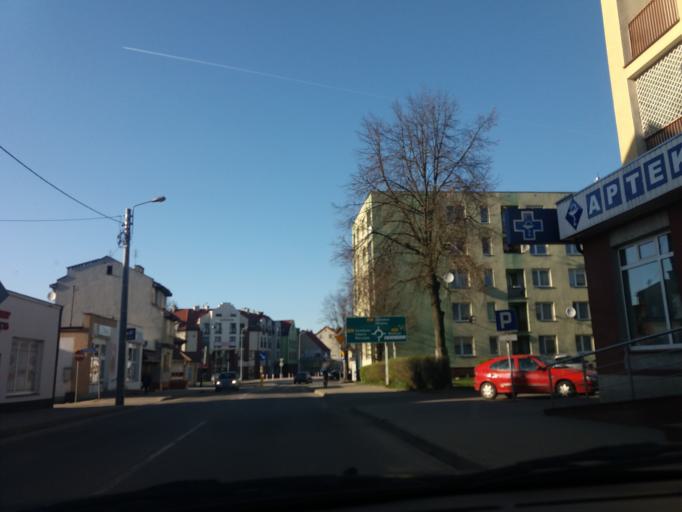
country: PL
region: Warmian-Masurian Voivodeship
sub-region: Powiat nidzicki
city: Nidzica
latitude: 53.3606
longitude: 20.4259
